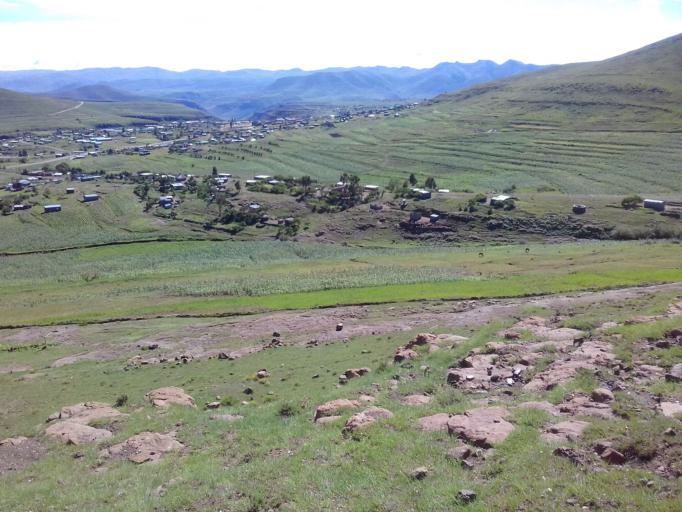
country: LS
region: Thaba-Tseka
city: Thaba-Tseka
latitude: -29.5252
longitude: 28.5840
